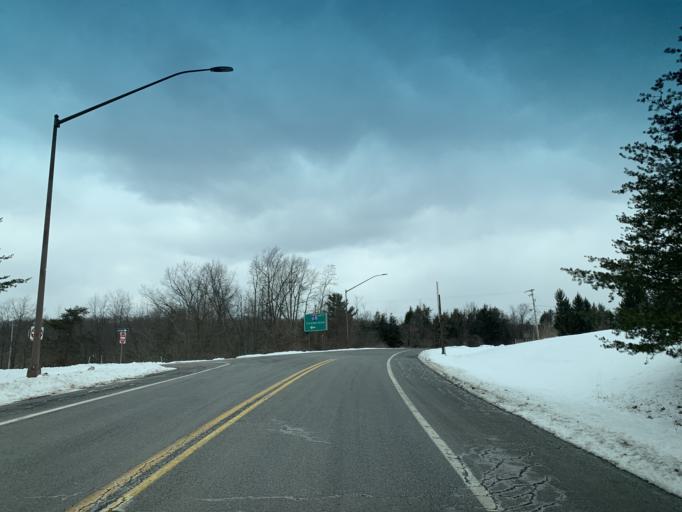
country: US
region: West Virginia
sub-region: Morgan County
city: Berkeley Springs
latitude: 39.6691
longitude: -78.4415
